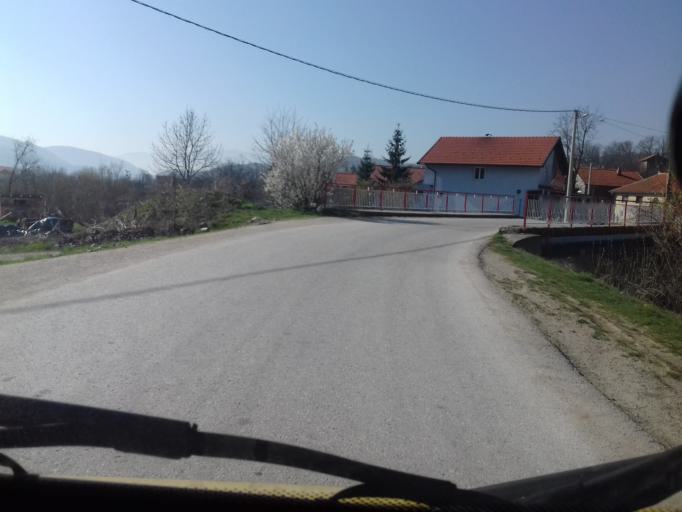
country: BA
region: Federation of Bosnia and Herzegovina
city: Travnik
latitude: 44.2565
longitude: 17.7467
